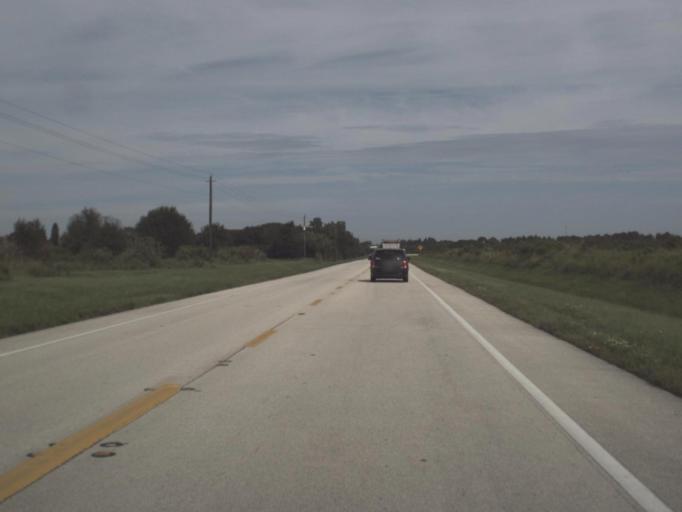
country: US
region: Florida
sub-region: DeSoto County
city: Nocatee
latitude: 27.0651
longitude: -81.7922
